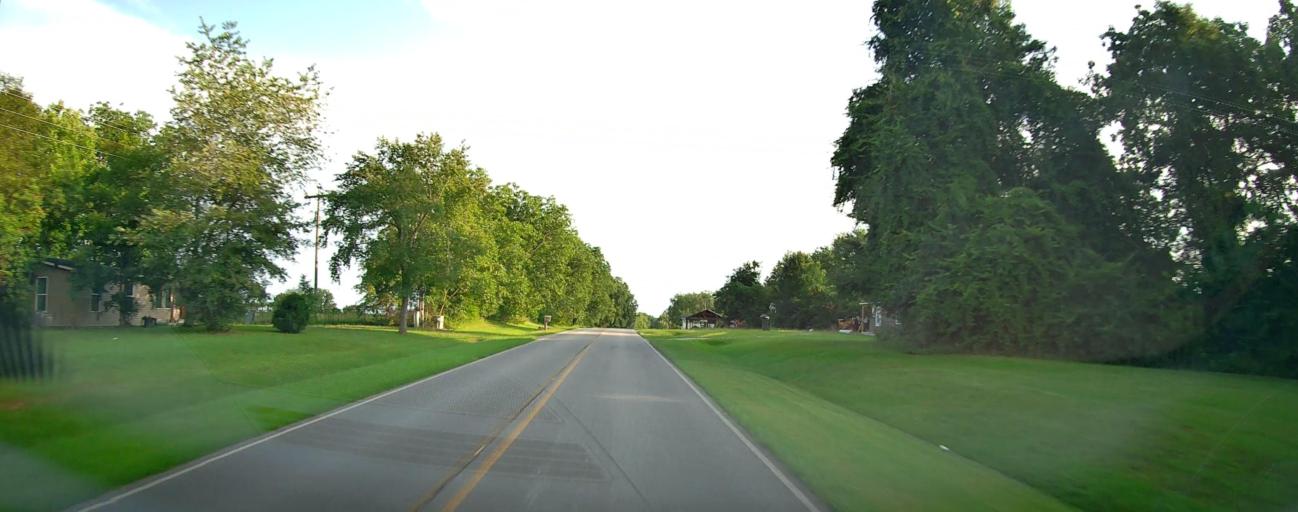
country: US
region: Georgia
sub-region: Peach County
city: Byron
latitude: 32.6848
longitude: -83.8573
